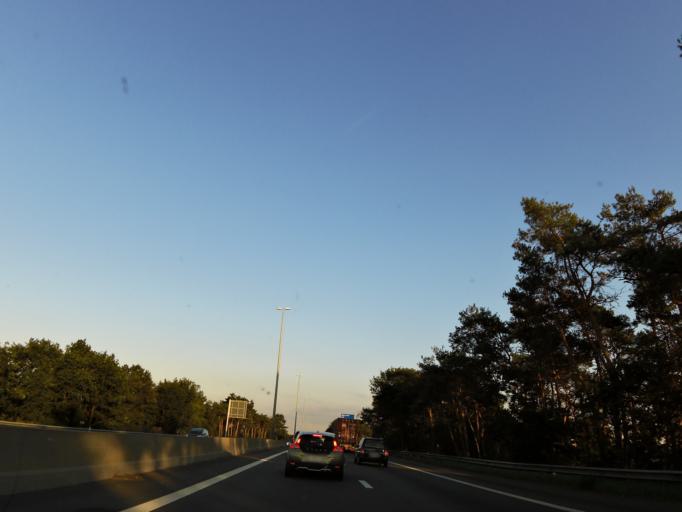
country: BE
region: Flanders
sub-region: Provincie Antwerpen
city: Vorselaar
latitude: 51.1680
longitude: 4.7801
